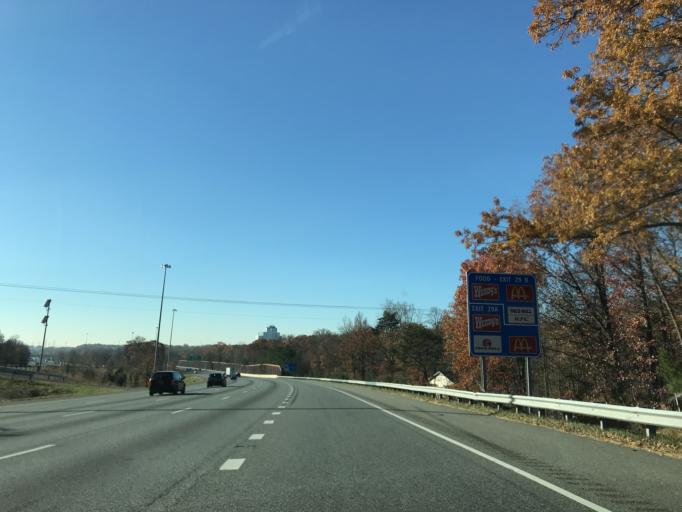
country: US
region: Maryland
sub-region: Prince George's County
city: Calverton
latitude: 39.0598
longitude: -76.9248
